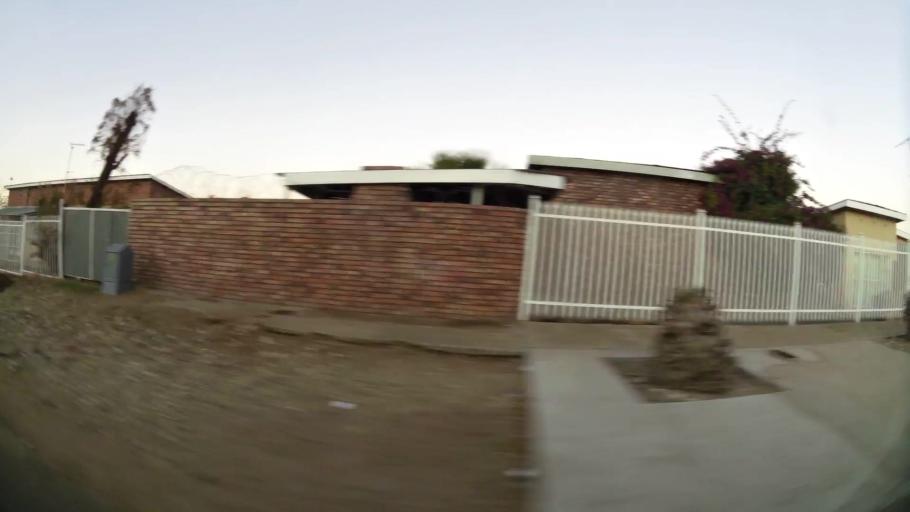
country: ZA
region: Northern Cape
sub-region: Frances Baard District Municipality
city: Kimberley
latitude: -28.7208
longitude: 24.7676
